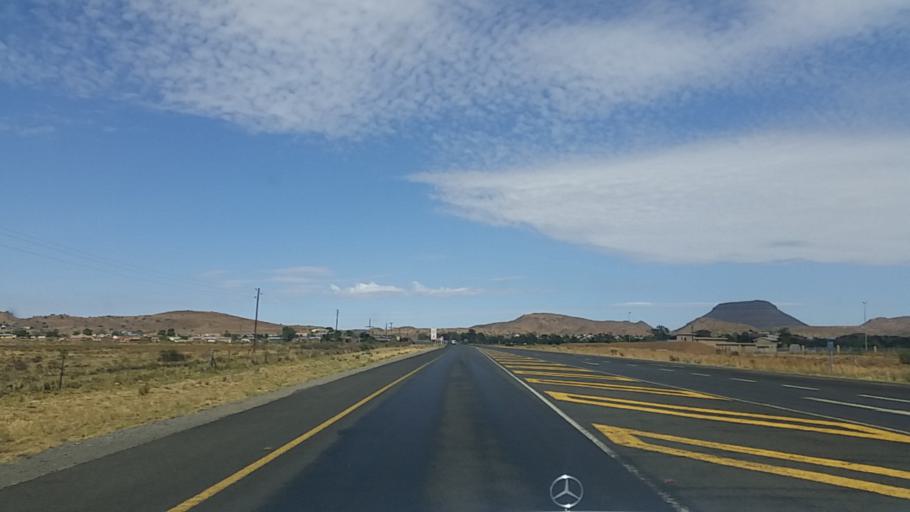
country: ZA
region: Northern Cape
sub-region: Pixley ka Seme District Municipality
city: Colesberg
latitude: -30.7039
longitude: 25.1181
